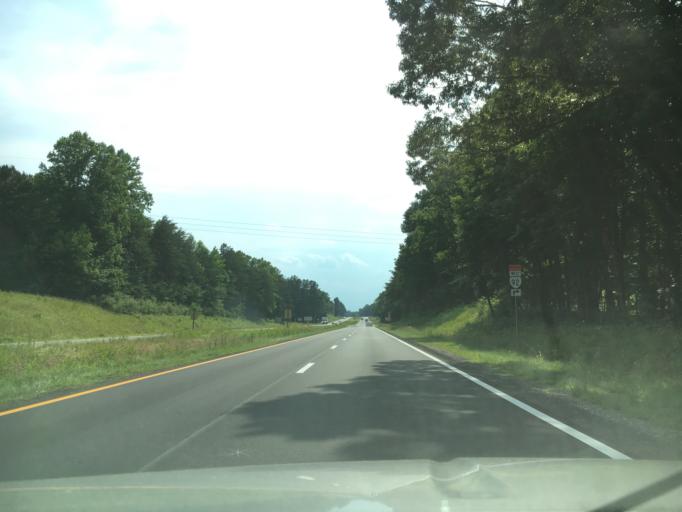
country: US
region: Virginia
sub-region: Halifax County
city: Halifax
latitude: 36.8184
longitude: -78.7322
